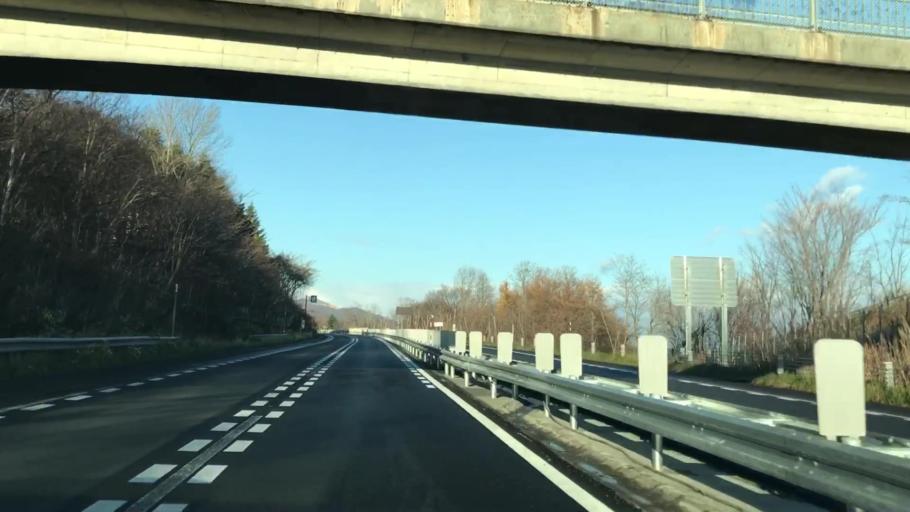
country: JP
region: Hokkaido
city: Otaru
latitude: 43.1343
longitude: 141.1707
